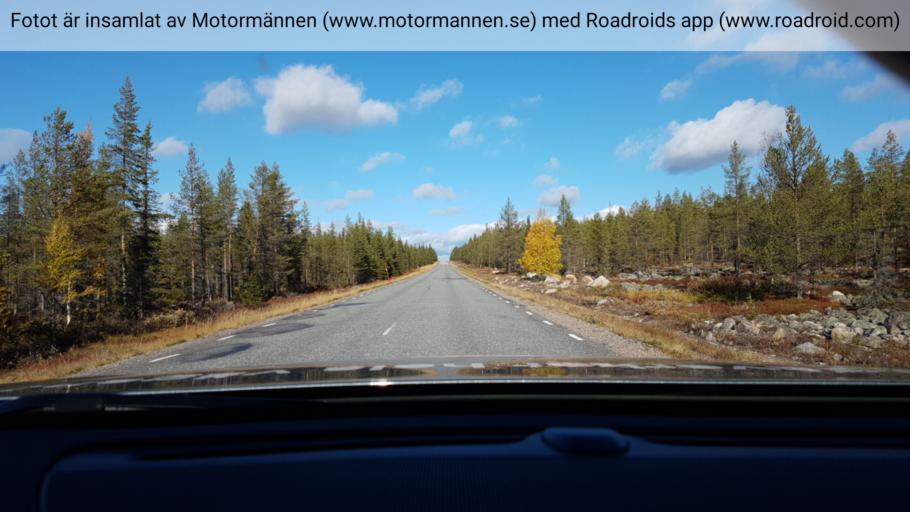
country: SE
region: Norrbotten
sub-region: Arjeplogs Kommun
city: Arjeplog
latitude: 65.8241
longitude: 18.4375
